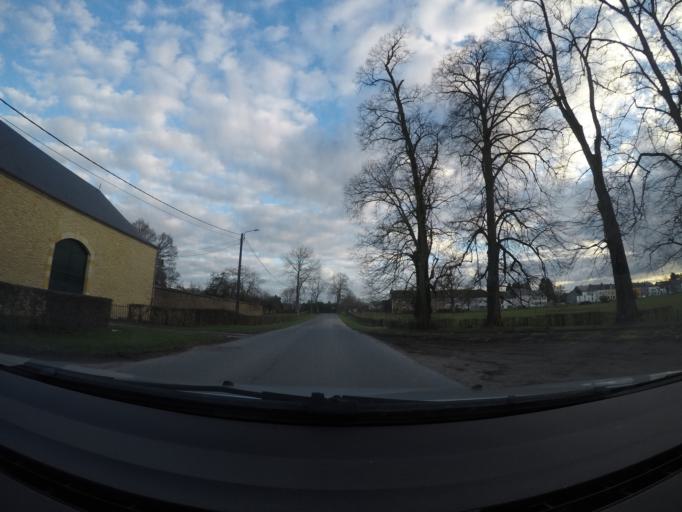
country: BE
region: Wallonia
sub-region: Province du Luxembourg
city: Etalle
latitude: 49.6759
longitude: 5.5653
